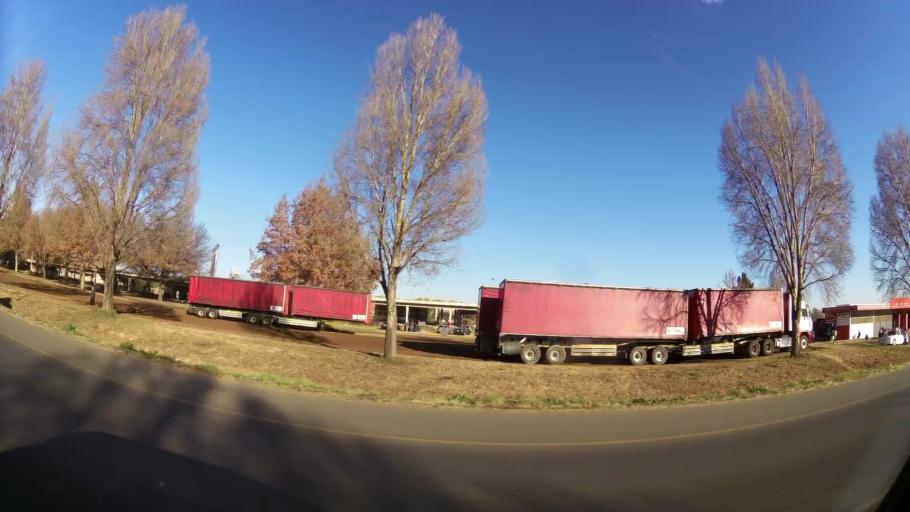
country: ZA
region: Gauteng
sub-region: Ekurhuleni Metropolitan Municipality
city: Germiston
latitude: -26.3115
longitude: 28.1390
